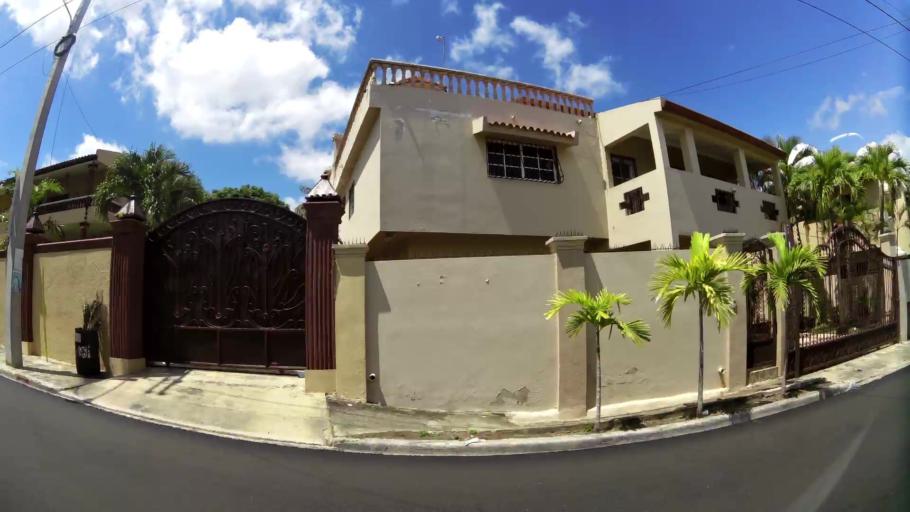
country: DO
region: Santiago
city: Santiago de los Caballeros
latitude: 19.4697
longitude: -70.6738
